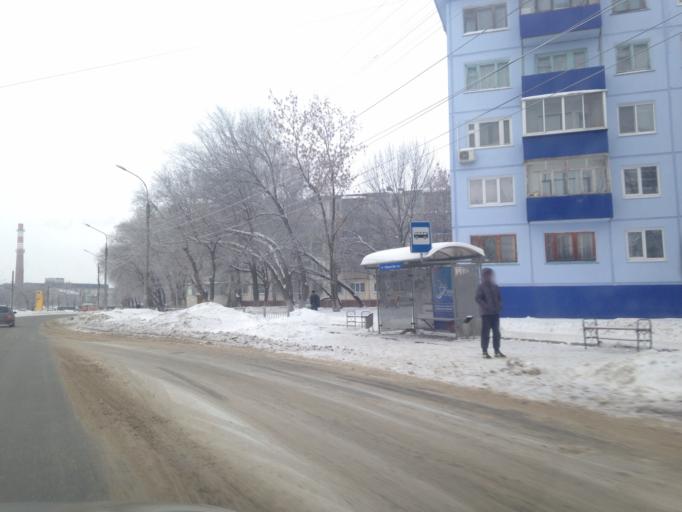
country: RU
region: Ulyanovsk
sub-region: Ulyanovskiy Rayon
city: Ulyanovsk
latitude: 54.2989
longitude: 48.3397
